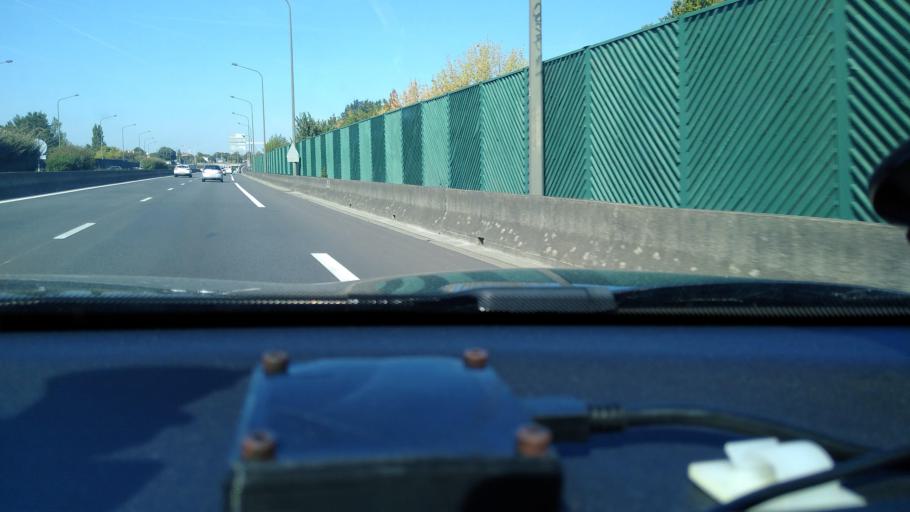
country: FR
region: Midi-Pyrenees
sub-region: Departement de la Haute-Garonne
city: Colomiers
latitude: 43.5834
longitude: 1.3637
